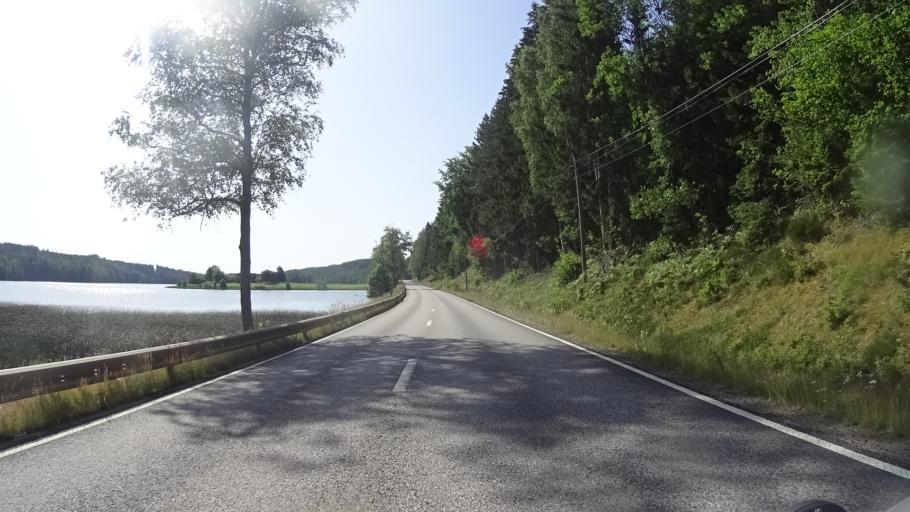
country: SE
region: Kalmar
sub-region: Vasterviks Kommun
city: Overum
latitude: 58.0072
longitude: 16.2686
